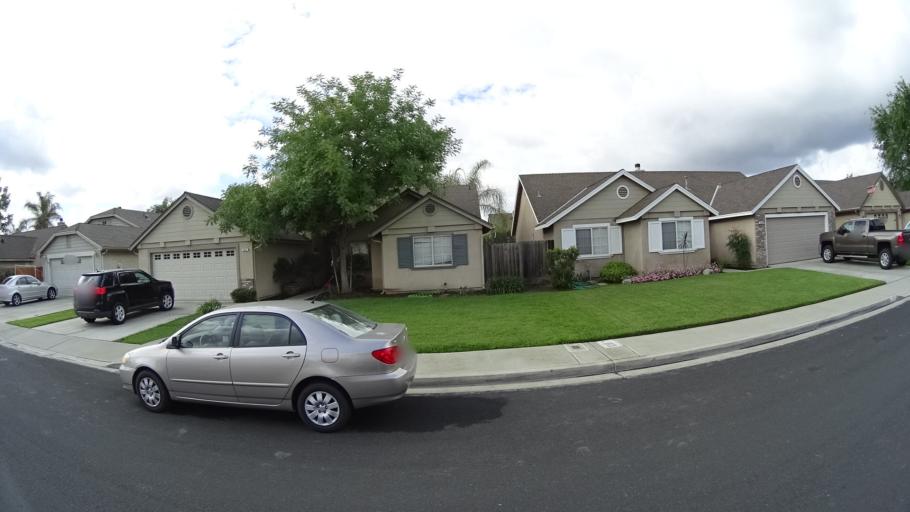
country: US
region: California
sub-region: Kings County
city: Lucerne
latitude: 36.3671
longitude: -119.6530
